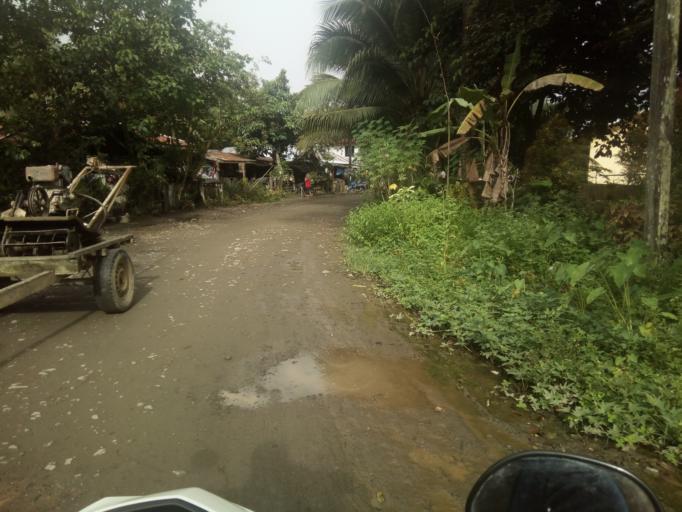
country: PH
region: Caraga
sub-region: Province of Agusan del Sur
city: Santa Josefa
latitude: 8.0206
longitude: 125.9942
